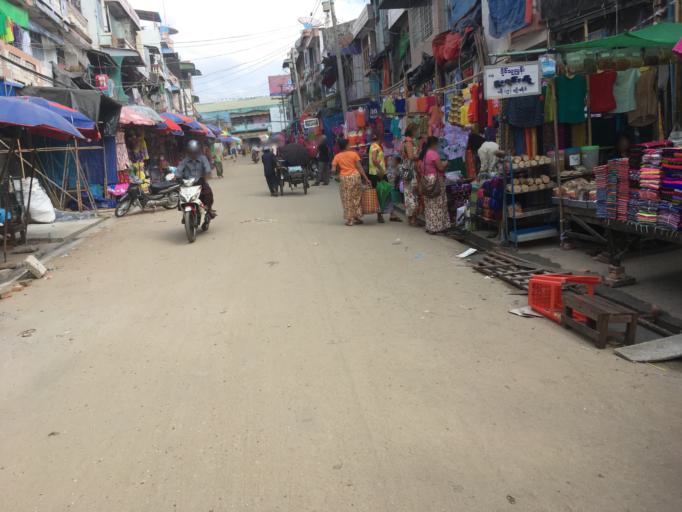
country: MM
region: Mon
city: Mawlamyine
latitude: 16.4935
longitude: 97.6205
